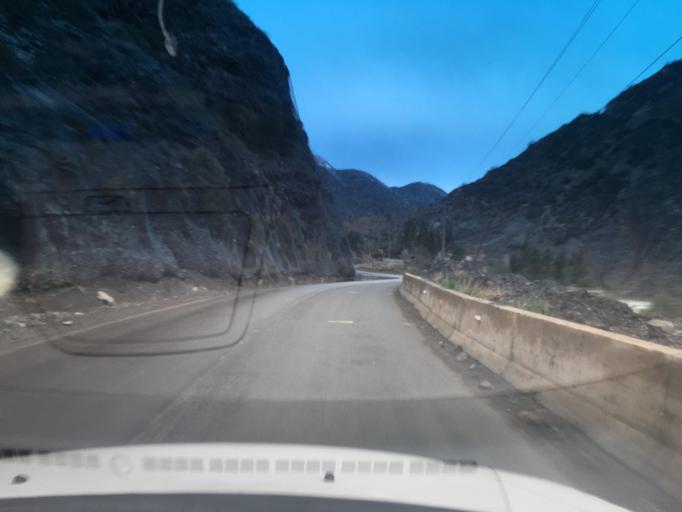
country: CL
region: Santiago Metropolitan
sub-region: Provincia de Cordillera
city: Puente Alto
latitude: -33.7403
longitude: -70.2956
